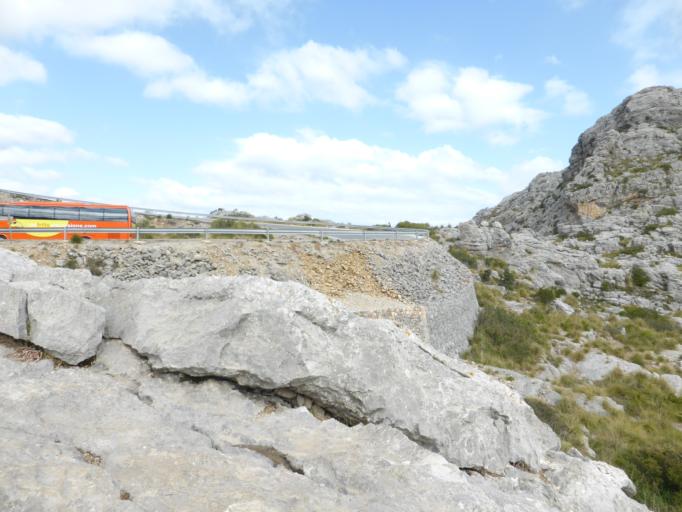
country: ES
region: Balearic Islands
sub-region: Illes Balears
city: Escorca
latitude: 39.8321
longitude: 2.8166
